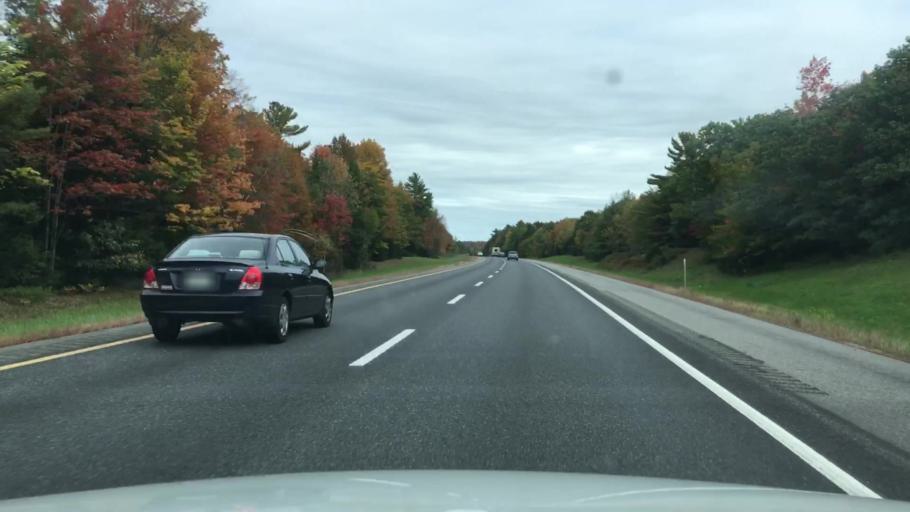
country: US
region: Maine
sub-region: Sagadahoc County
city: Richmond
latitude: 44.0484
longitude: -69.8914
